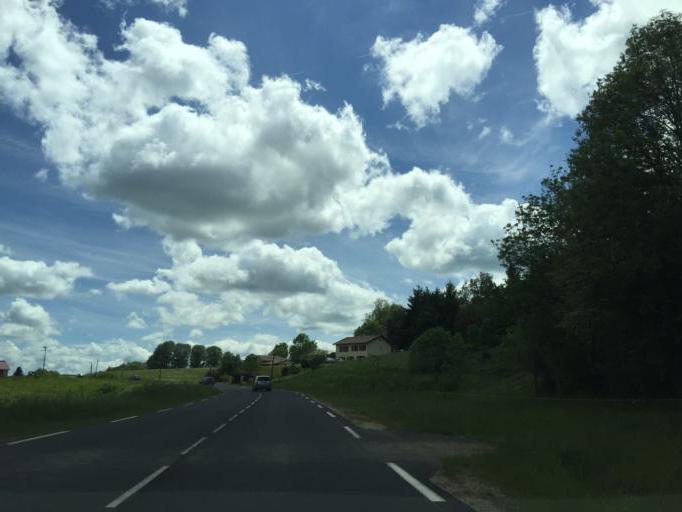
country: FR
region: Rhone-Alpes
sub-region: Departement de la Loire
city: Usson-en-Forez
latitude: 45.5181
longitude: 3.9116
